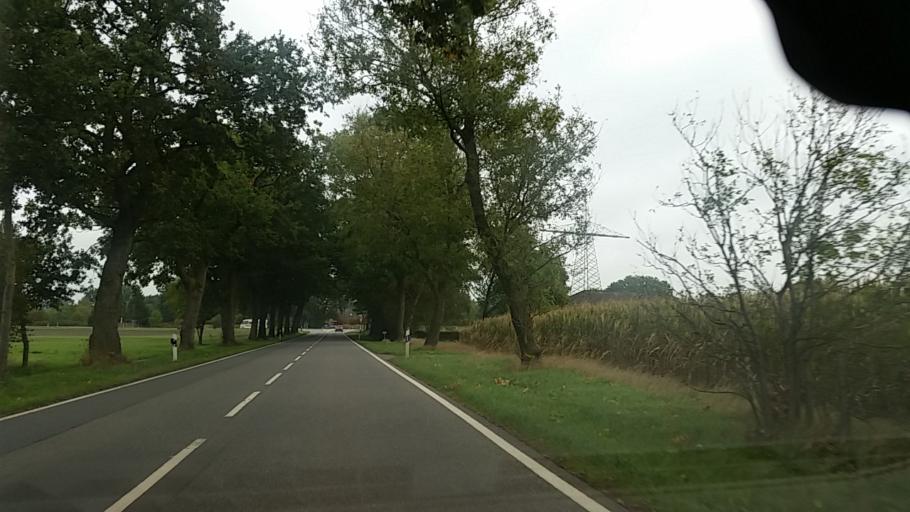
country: DE
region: Schleswig-Holstein
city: Hasenmoor
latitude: 53.8979
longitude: 9.9789
